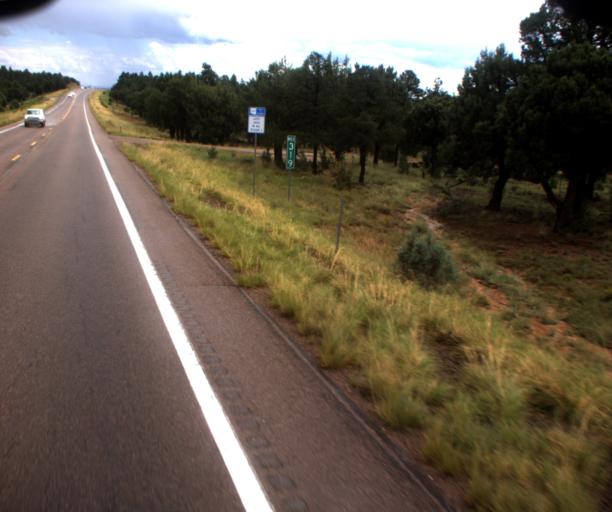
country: US
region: Arizona
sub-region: Navajo County
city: Heber-Overgaard
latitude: 34.3673
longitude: -110.3723
